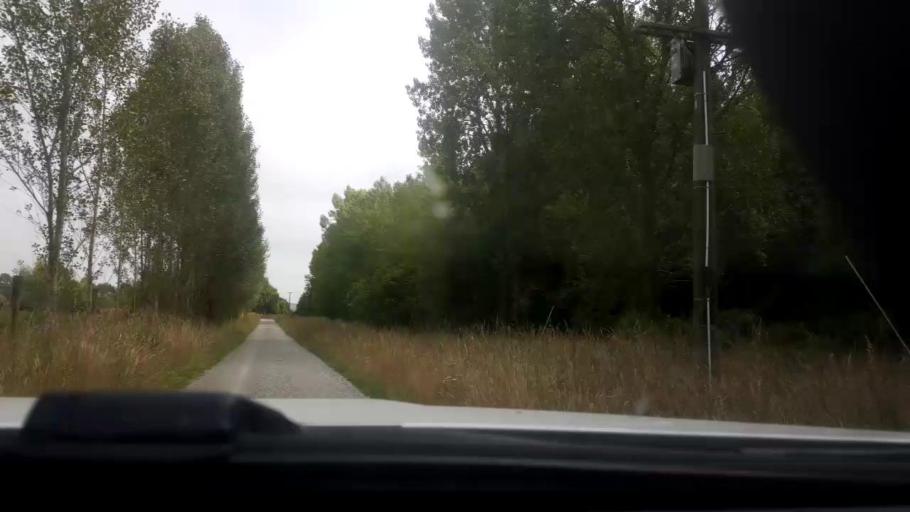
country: NZ
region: Canterbury
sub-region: Timaru District
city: Pleasant Point
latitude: -44.3271
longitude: 171.1963
